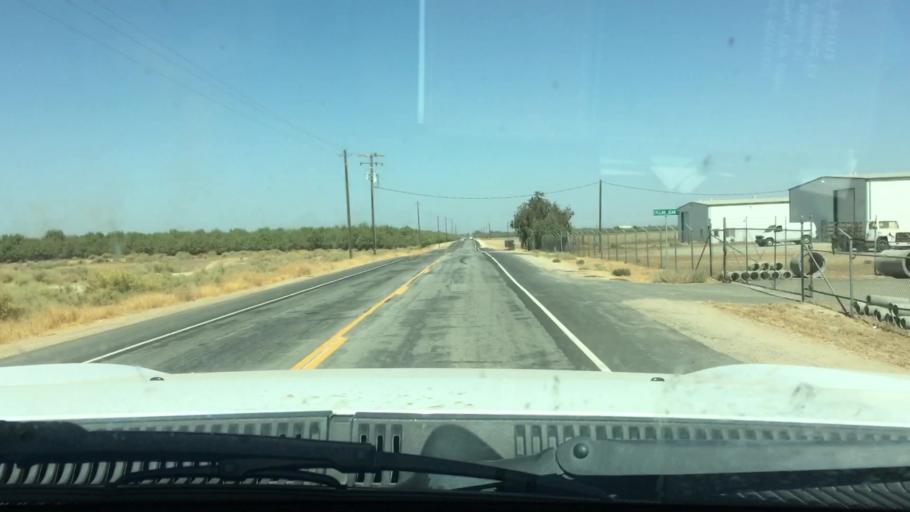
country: US
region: California
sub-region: Kern County
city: Shafter
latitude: 35.4432
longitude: -119.2789
